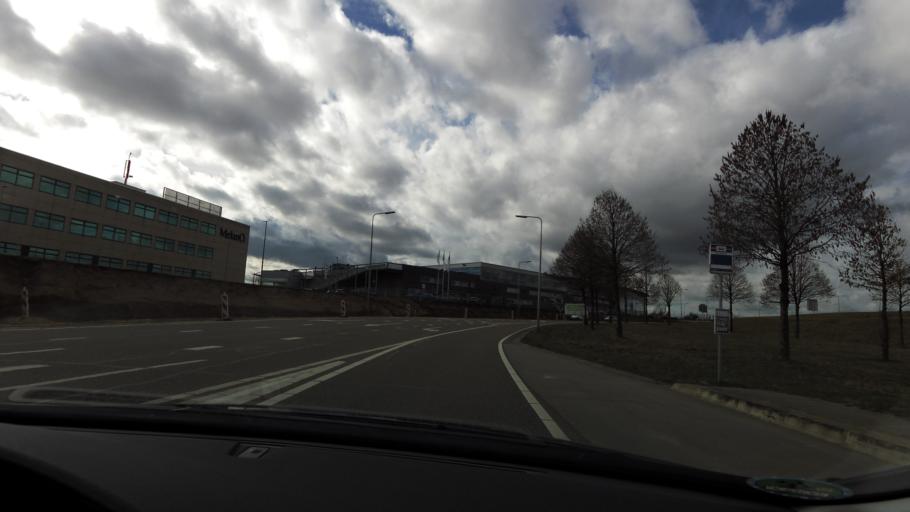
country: NL
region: Limburg
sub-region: Gemeente Stein
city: Elsloo
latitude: 50.9249
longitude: 5.7773
